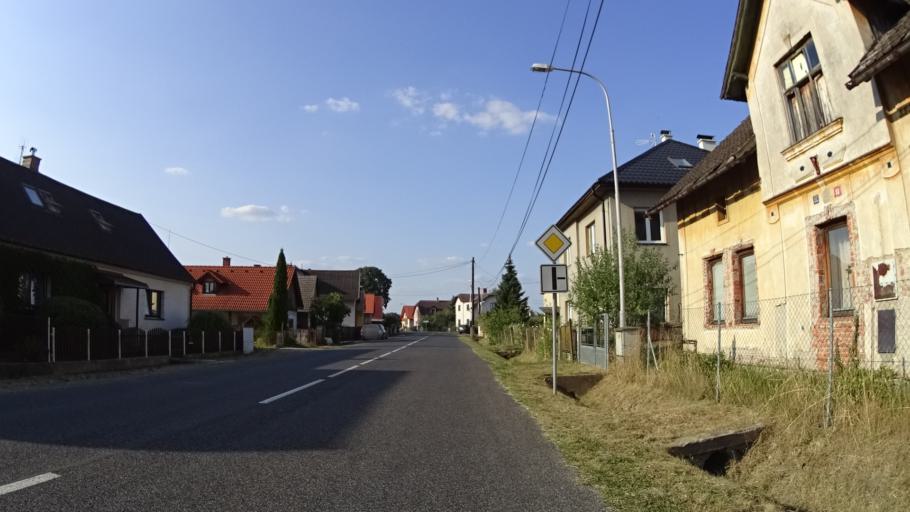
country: CZ
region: Central Bohemia
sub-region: Okres Mlada Boleslav
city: Zd'ar
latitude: 50.5573
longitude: 15.0685
